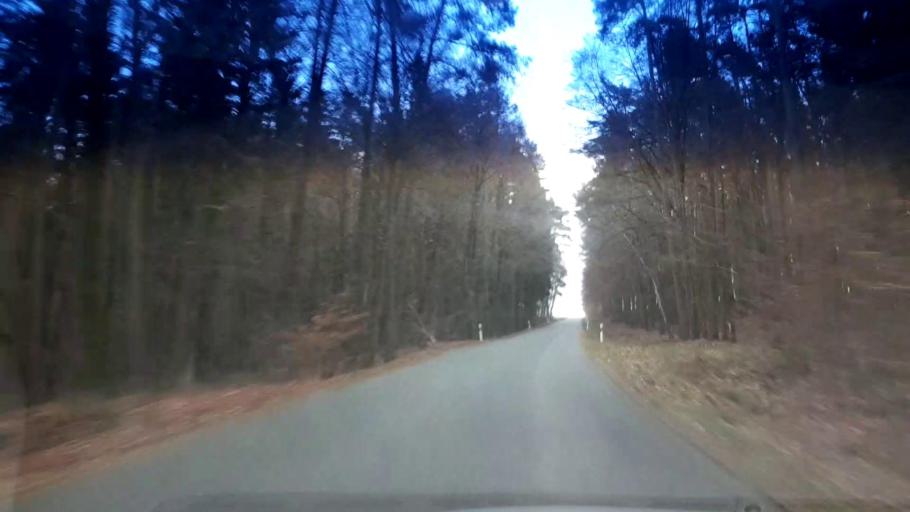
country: DE
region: Bavaria
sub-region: Upper Franconia
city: Hallerndorf
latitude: 49.7703
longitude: 10.9215
